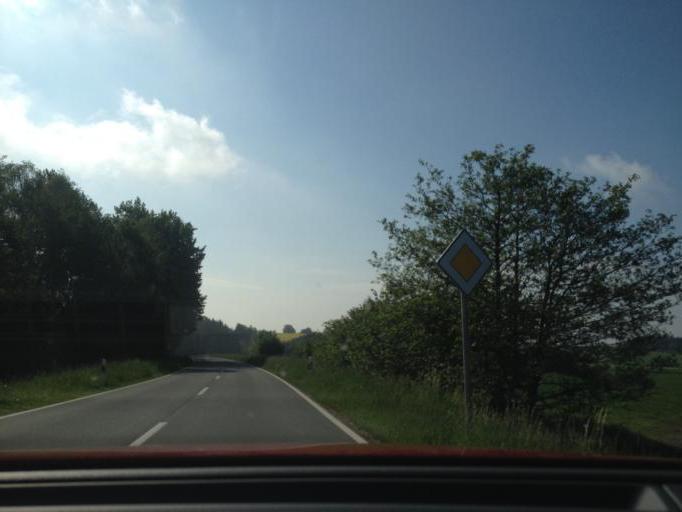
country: DE
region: Bavaria
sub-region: Upper Palatinate
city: Kirchenthumbach
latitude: 49.7656
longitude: 11.6792
